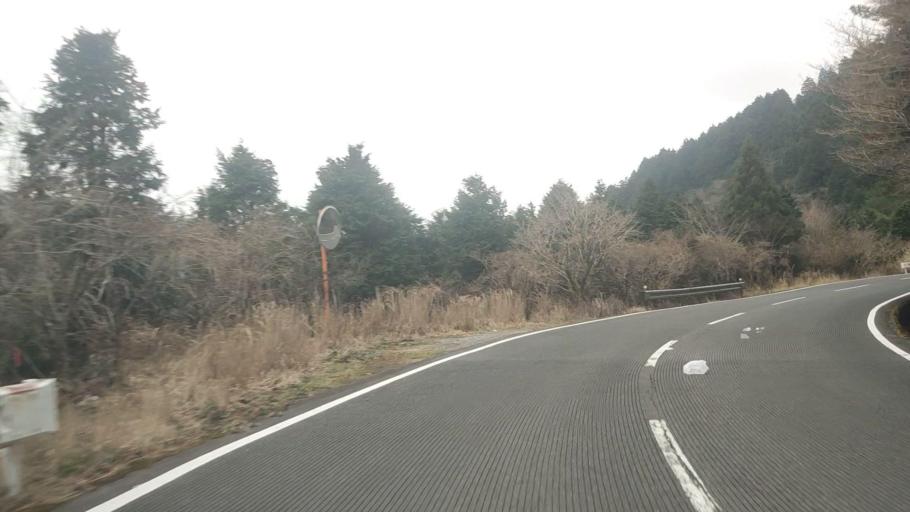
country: JP
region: Nagasaki
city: Shimabara
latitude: 32.7677
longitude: 130.2721
